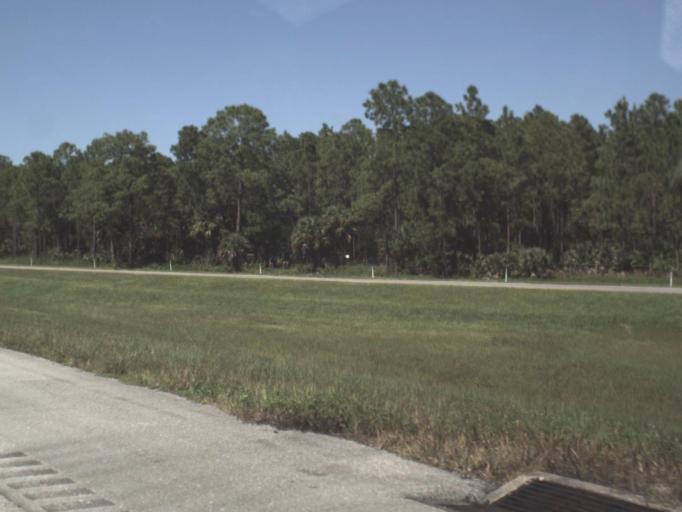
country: US
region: Florida
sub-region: Collier County
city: Golden Gate
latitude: 26.1614
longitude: -81.6898
